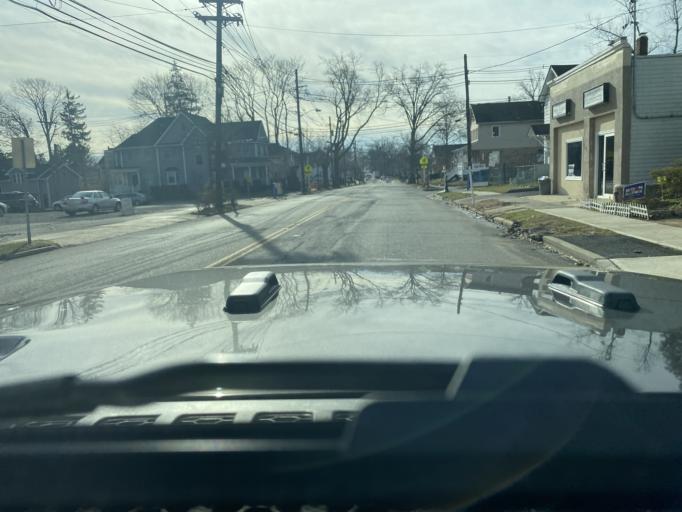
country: US
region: New Jersey
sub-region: Middlesex County
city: Metuchen
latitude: 40.5326
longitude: -74.3589
